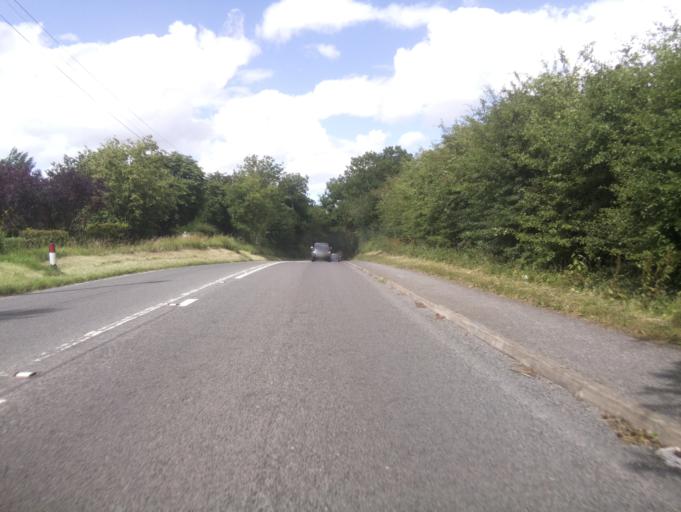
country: GB
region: England
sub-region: Nottinghamshire
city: East Leake
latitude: 52.8462
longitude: -1.1423
